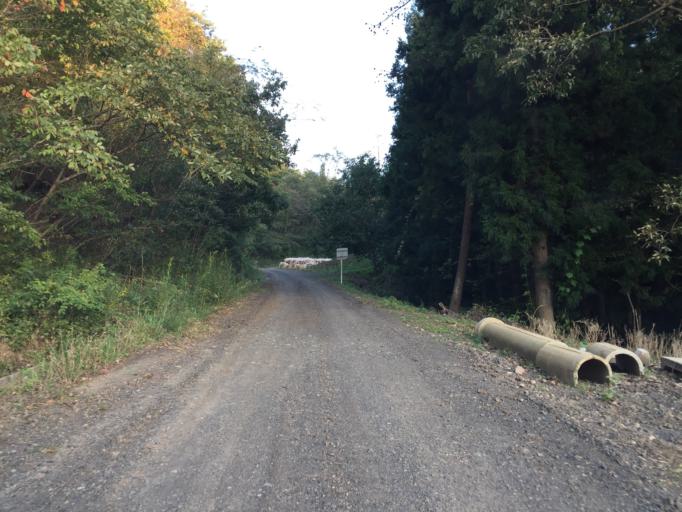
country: JP
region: Fukushima
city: Yanagawamachi-saiwaicho
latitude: 37.8439
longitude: 140.6233
